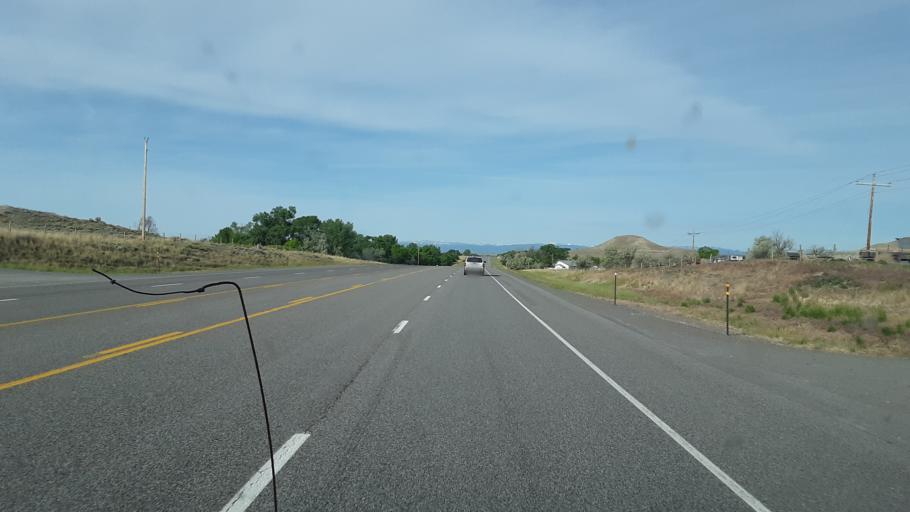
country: US
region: Wyoming
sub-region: Fremont County
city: Riverton
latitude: 43.1290
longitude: -108.3089
